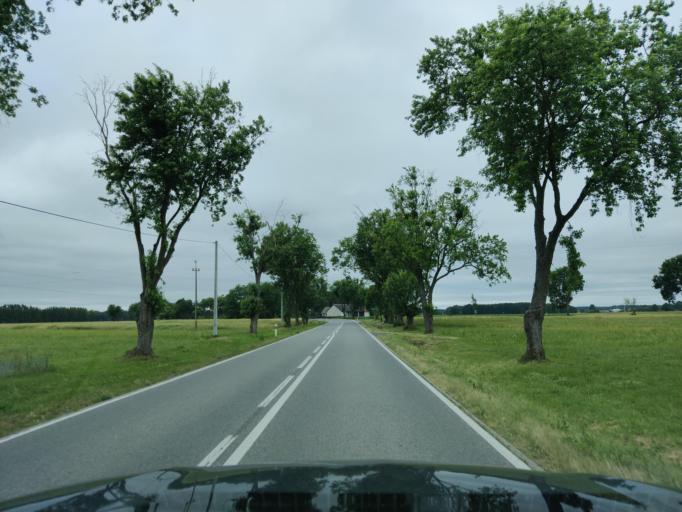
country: PL
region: Masovian Voivodeship
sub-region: Powiat ostrolecki
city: Czarnia
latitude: 53.3246
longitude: 21.1427
